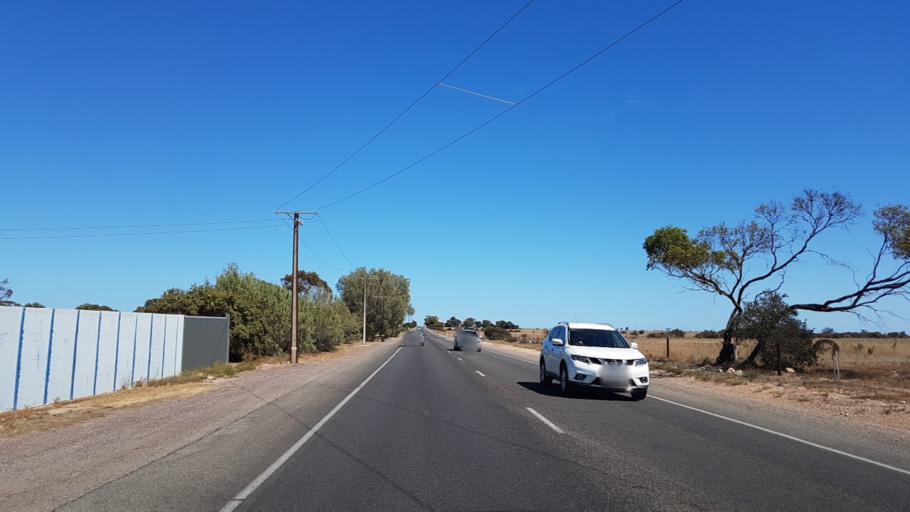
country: AU
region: South Australia
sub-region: Copper Coast
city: Kadina
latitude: -33.9524
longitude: 137.6804
